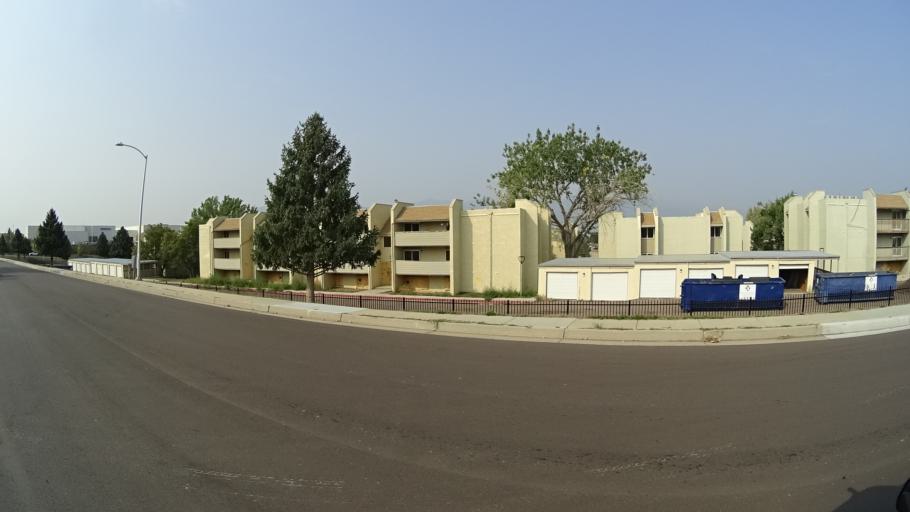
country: US
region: Colorado
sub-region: El Paso County
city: Stratmoor
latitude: 38.8191
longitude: -104.7534
